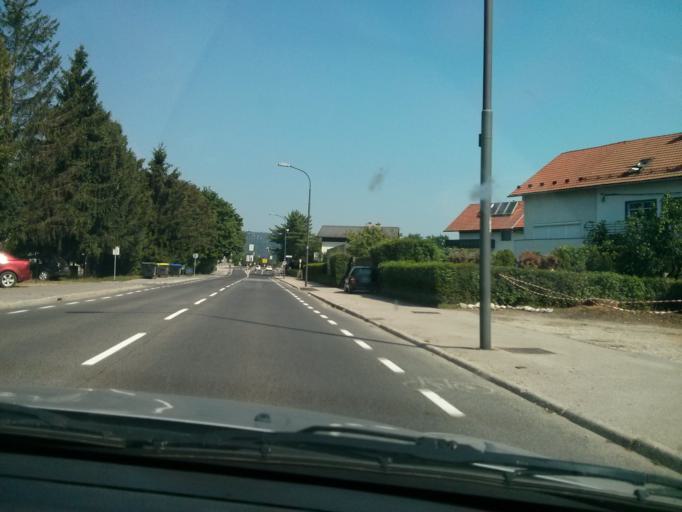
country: SI
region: Ljubljana
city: Ljubljana
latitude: 46.0750
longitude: 14.4751
